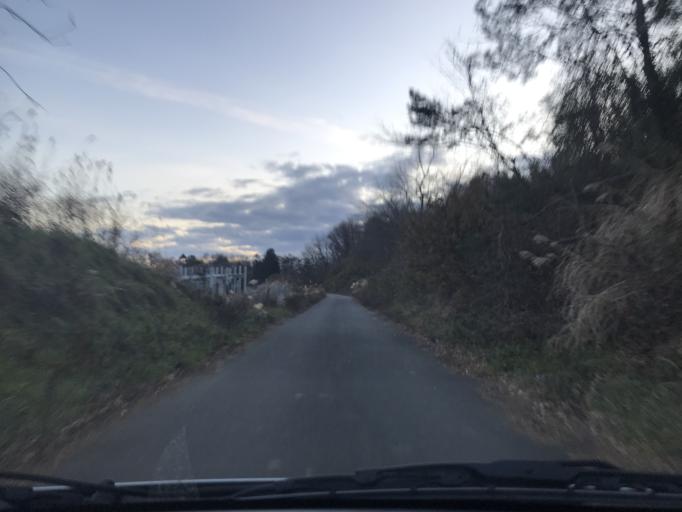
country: JP
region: Iwate
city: Ichinoseki
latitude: 38.8318
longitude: 141.0943
